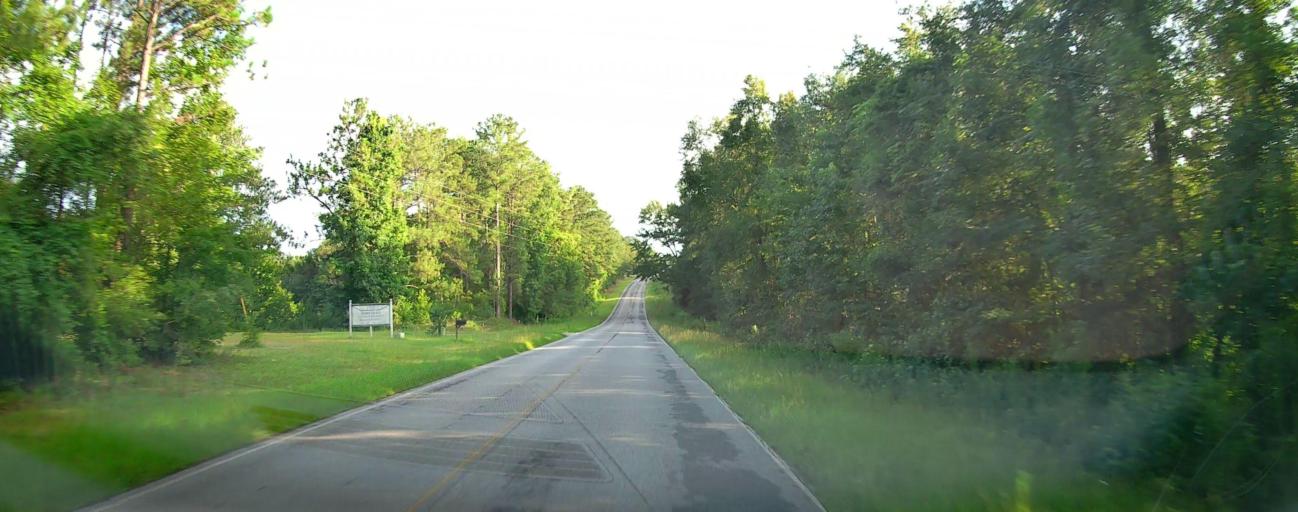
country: US
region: Georgia
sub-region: Bibb County
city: West Point
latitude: 32.7110
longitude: -83.8464
